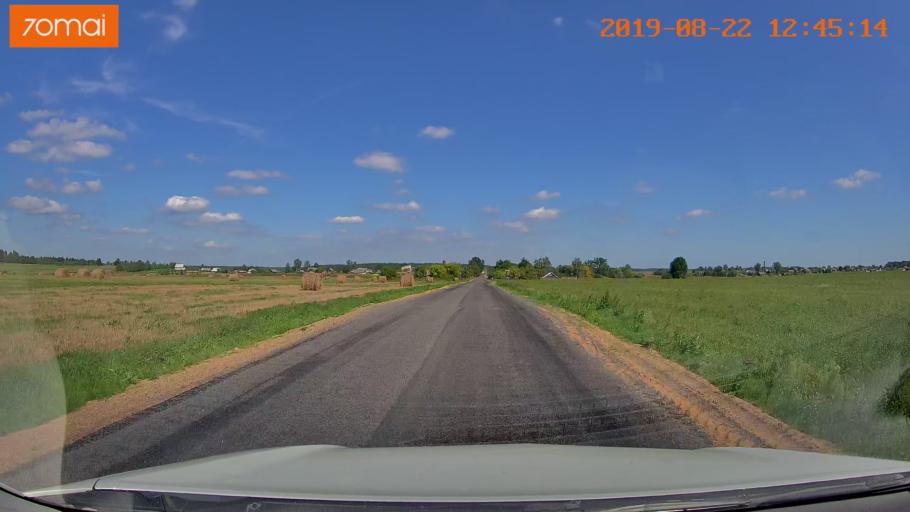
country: BY
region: Minsk
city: Prawdzinski
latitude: 53.4555
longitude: 27.6179
